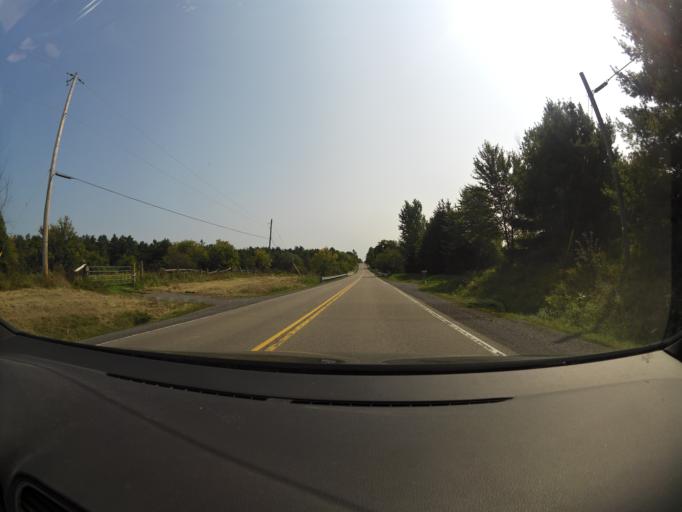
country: CA
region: Ontario
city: Arnprior
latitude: 45.4395
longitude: -76.1792
